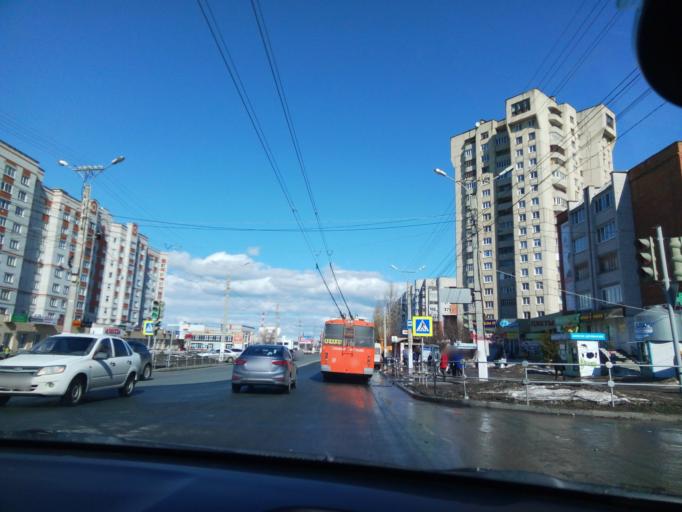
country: RU
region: Chuvashia
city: Novyye Lapsary
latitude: 56.1178
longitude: 47.1835
